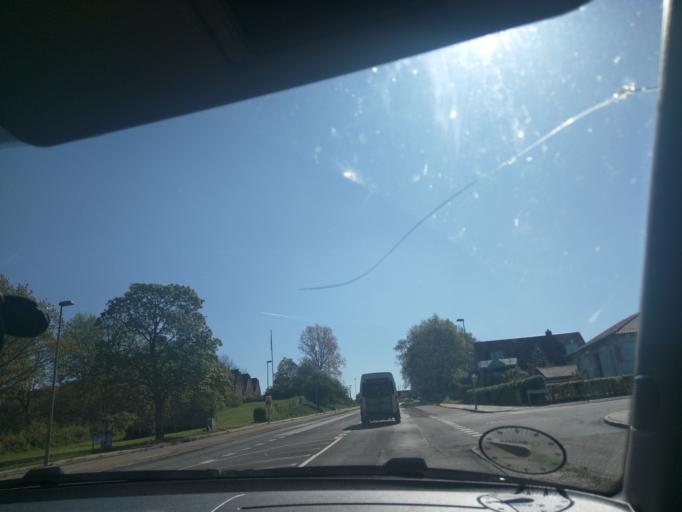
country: DK
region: Central Jutland
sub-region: Viborg Kommune
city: Viborg
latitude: 56.4493
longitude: 9.4263
